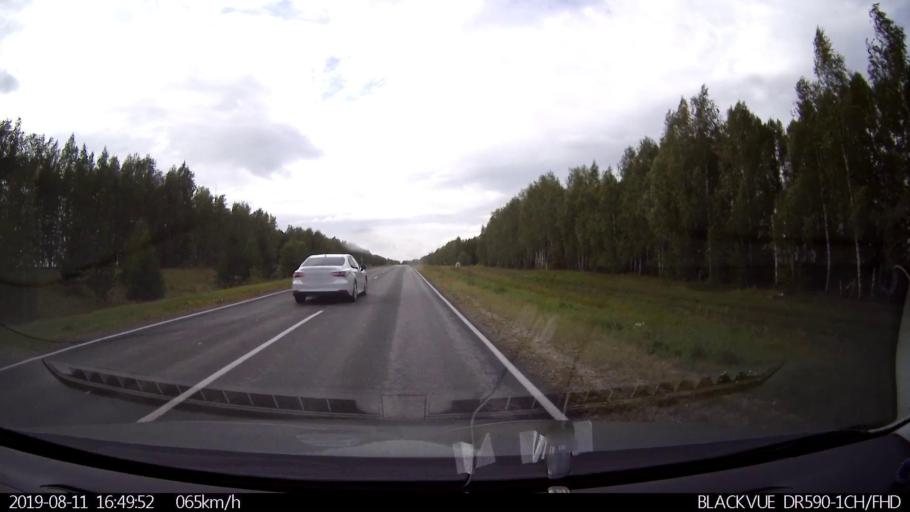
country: RU
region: Ulyanovsk
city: Mayna
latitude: 54.2241
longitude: 47.6936
